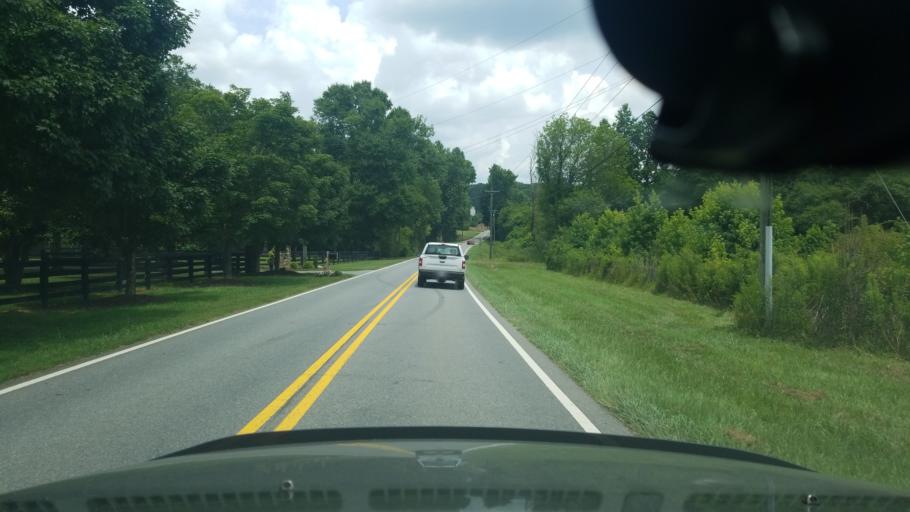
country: US
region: Georgia
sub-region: Forsyth County
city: Cumming
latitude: 34.1932
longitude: -84.2300
